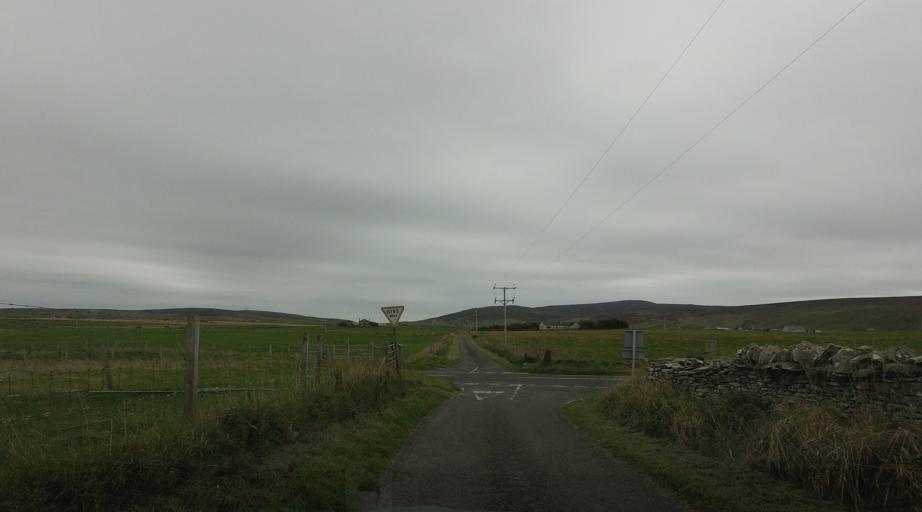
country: GB
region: Scotland
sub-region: Orkney Islands
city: Stromness
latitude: 58.9912
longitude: -3.1963
